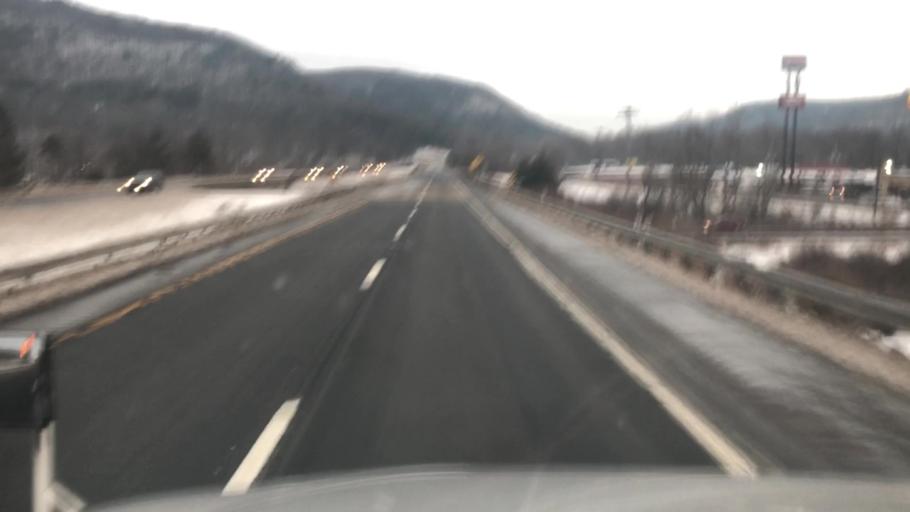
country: US
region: Pennsylvania
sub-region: Susquehanna County
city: Hallstead
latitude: 41.9680
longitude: -75.7392
